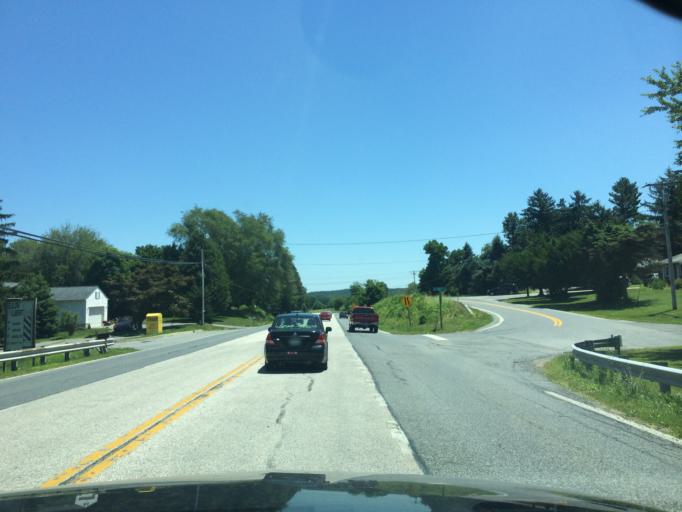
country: US
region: Maryland
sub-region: Carroll County
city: Eldersburg
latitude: 39.3960
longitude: -76.9200
